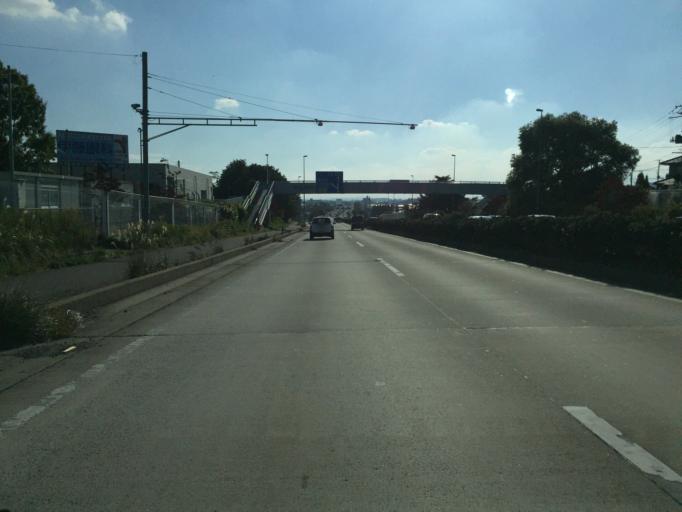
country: JP
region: Fukushima
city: Koriyama
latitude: 37.4244
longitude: 140.3580
